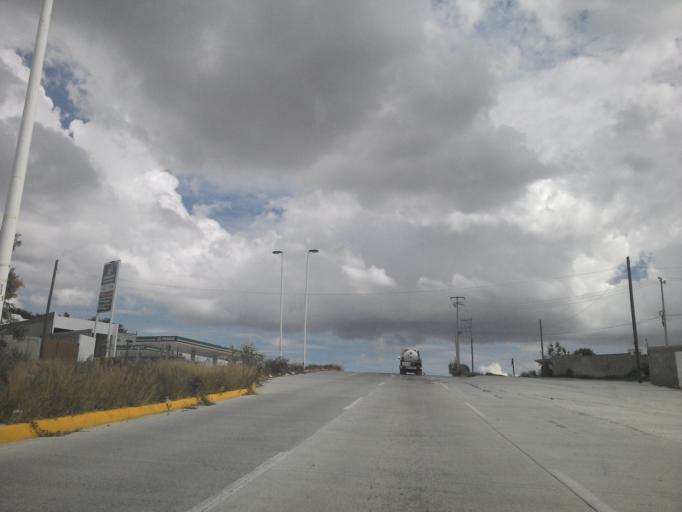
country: MX
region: Jalisco
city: Guadalajara
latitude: 20.6657
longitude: -103.4575
